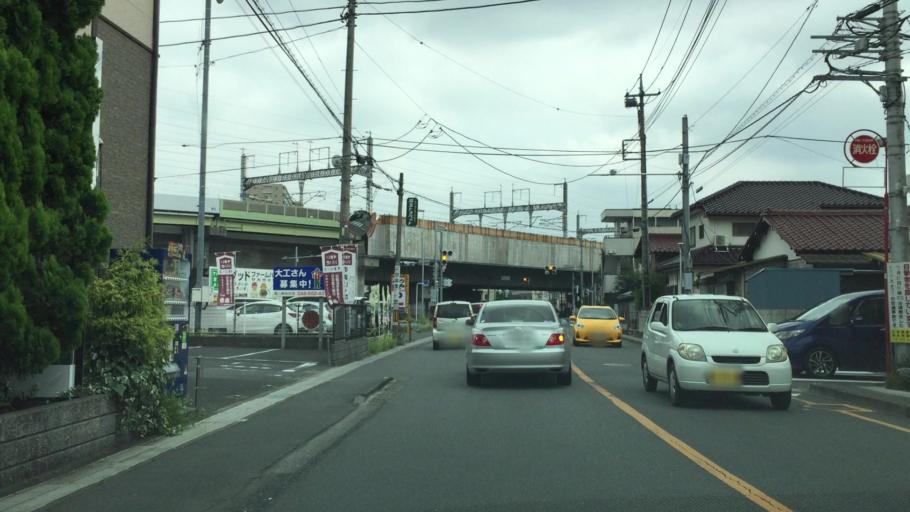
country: JP
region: Saitama
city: Ageoshimo
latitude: 35.9350
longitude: 139.6158
